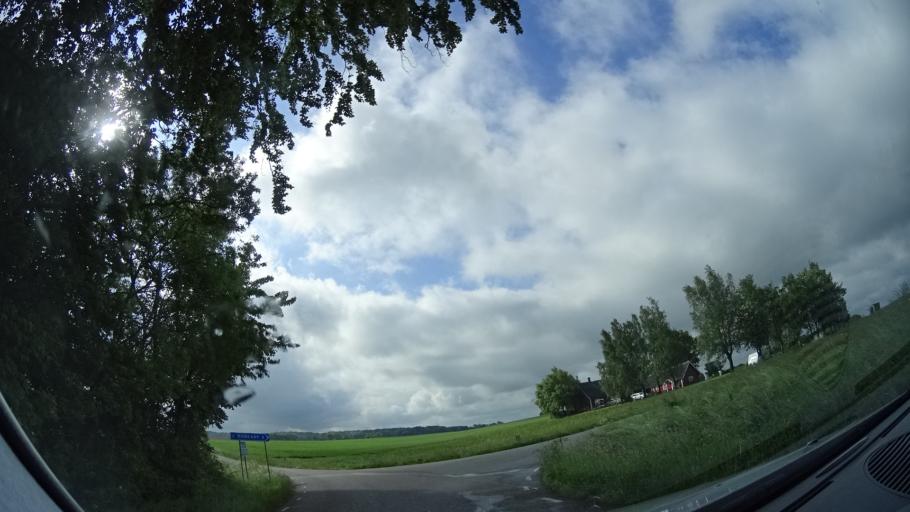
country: SE
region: Skane
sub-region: Eslovs Kommun
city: Stehag
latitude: 55.8752
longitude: 13.4458
